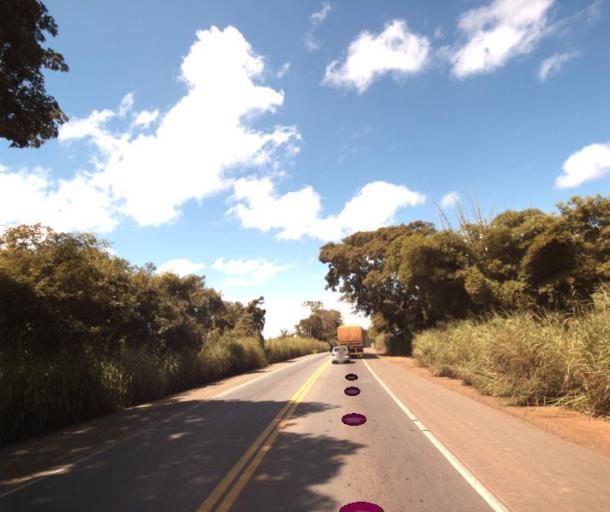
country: BR
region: Goias
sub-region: Jaragua
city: Jaragua
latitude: -15.7789
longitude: -49.3049
